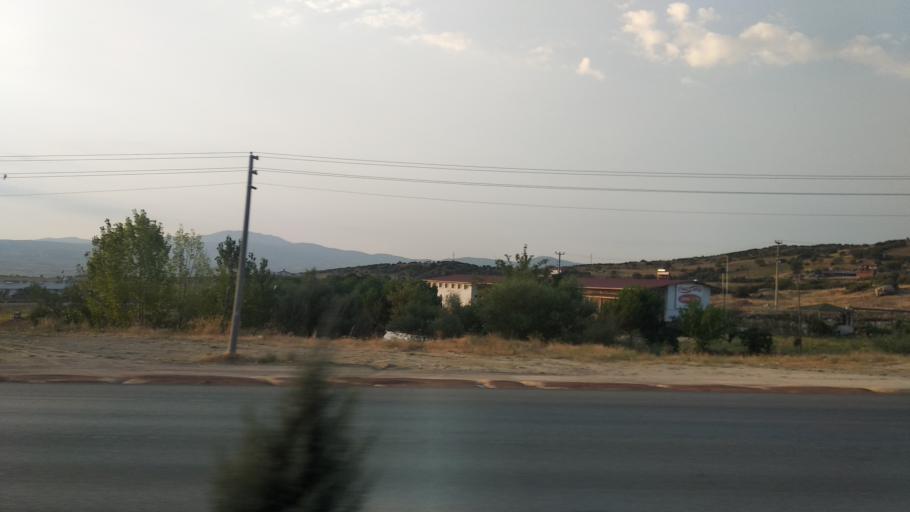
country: TR
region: Manisa
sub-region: Kula
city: Kula
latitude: 38.5490
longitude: 28.6752
